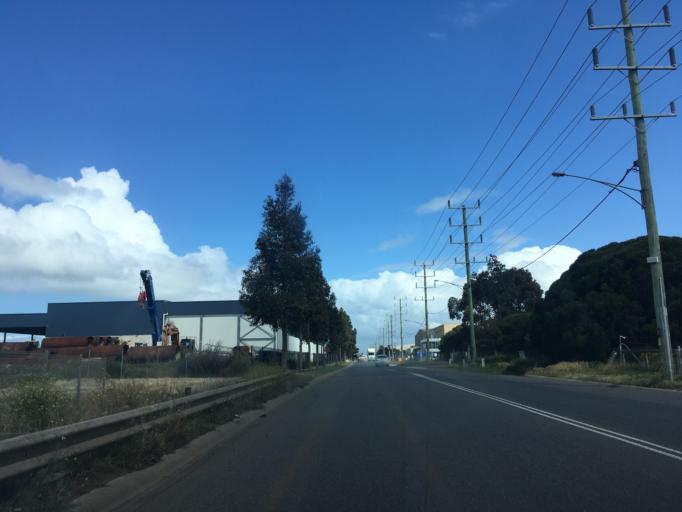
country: AU
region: Victoria
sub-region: Brimbank
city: Sunshine West
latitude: -37.8232
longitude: 144.7971
